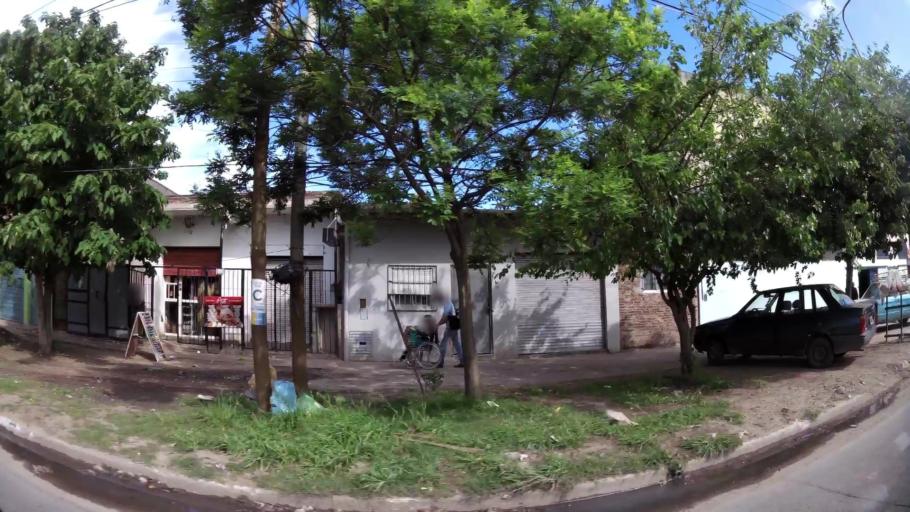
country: AR
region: Buenos Aires
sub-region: Partido de Almirante Brown
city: Adrogue
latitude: -34.7685
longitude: -58.3155
